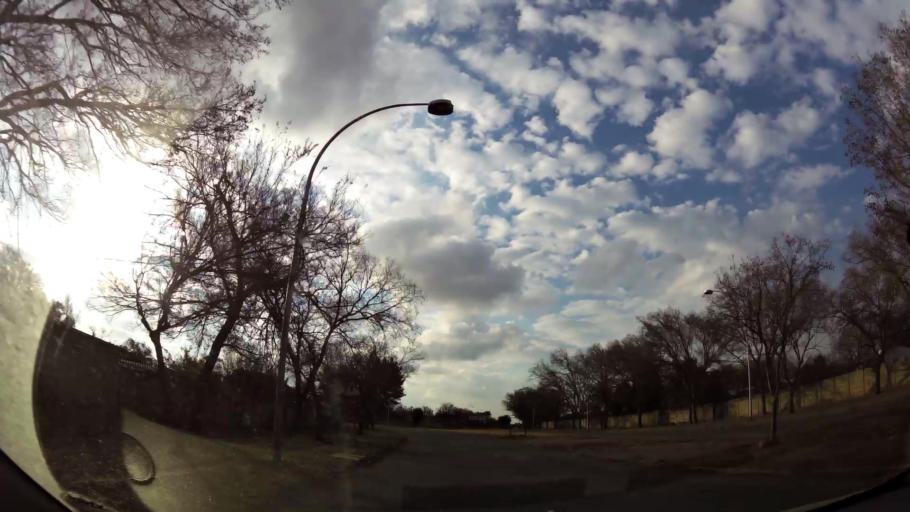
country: ZA
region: Orange Free State
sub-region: Fezile Dabi District Municipality
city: Sasolburg
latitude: -26.8155
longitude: 27.8092
